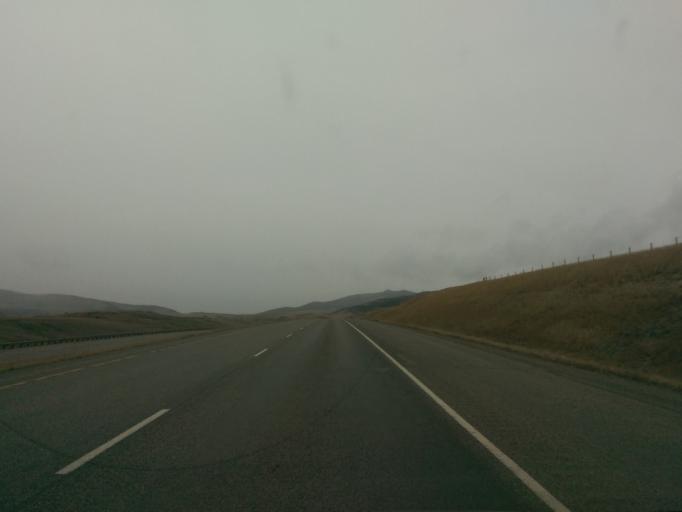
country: US
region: Montana
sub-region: Gallatin County
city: Three Forks
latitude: 45.9103
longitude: -111.7836
